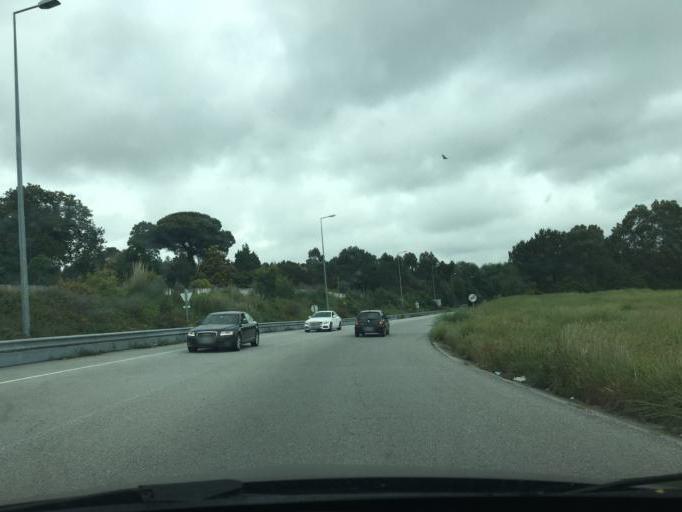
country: PT
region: Porto
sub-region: Matosinhos
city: Santa Cruz do Bispo
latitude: 41.2219
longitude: -8.6708
